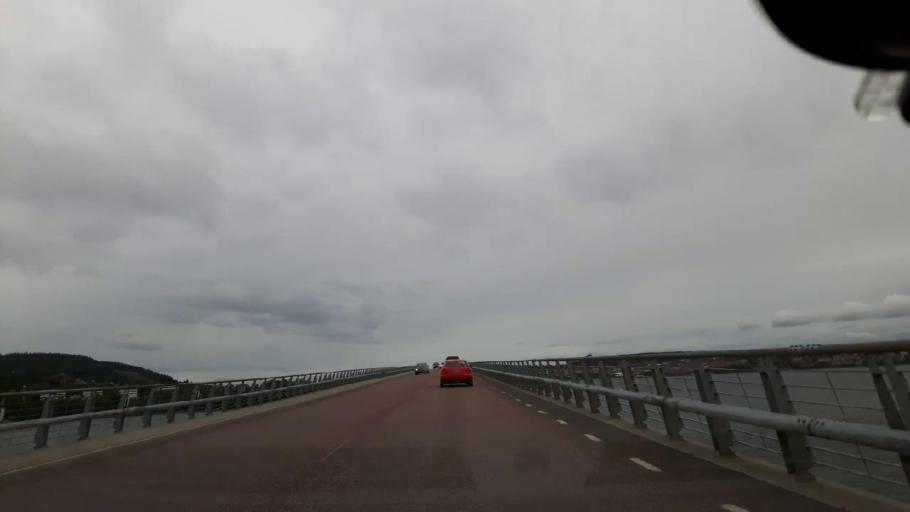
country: SE
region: Jaemtland
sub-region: OEstersunds Kommun
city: Ostersund
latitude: 63.1566
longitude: 14.5969
